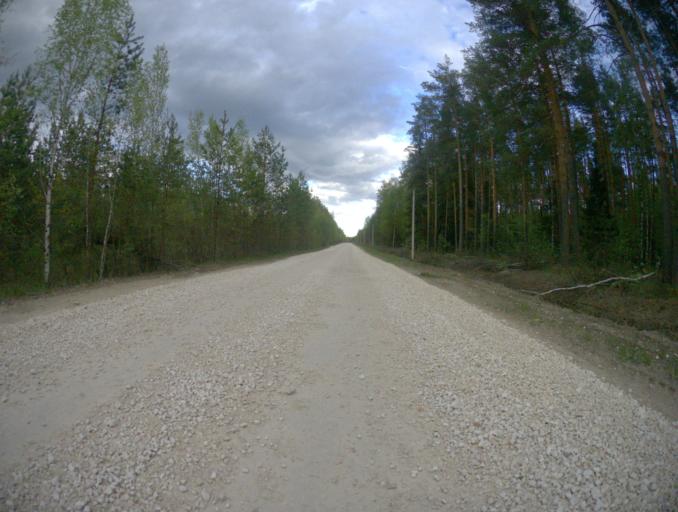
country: RU
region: Vladimir
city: Gusevskiy
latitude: 55.7205
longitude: 40.5897
